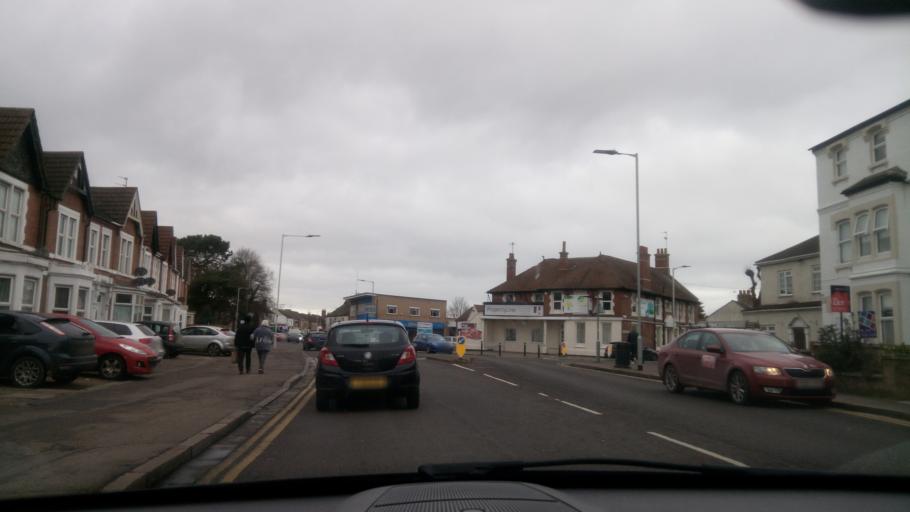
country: GB
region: England
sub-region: Peterborough
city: Peterborough
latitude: 52.5824
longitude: -0.2443
